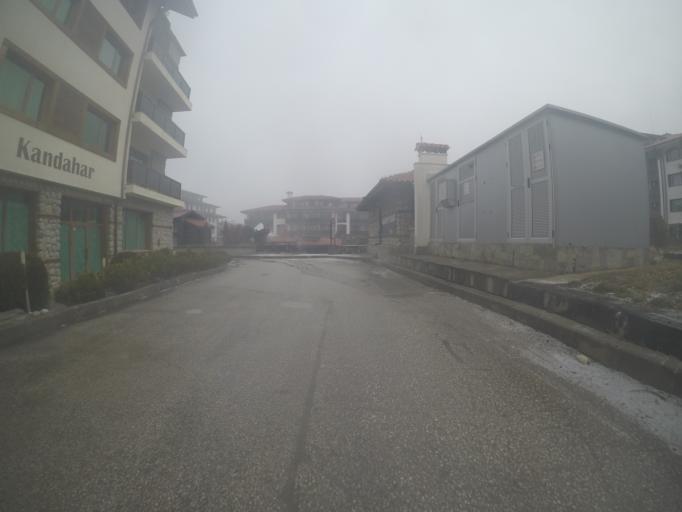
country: BG
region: Blagoevgrad
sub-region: Obshtina Bansko
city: Bansko
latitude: 41.8258
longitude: 23.4800
